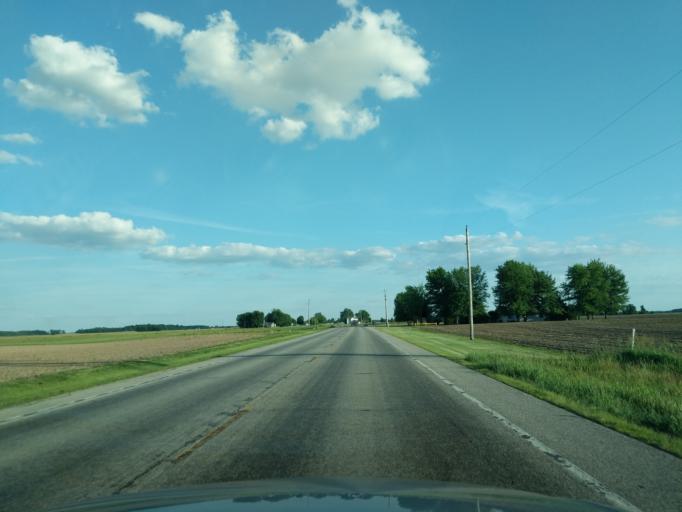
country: US
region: Indiana
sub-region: Huntington County
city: Warren
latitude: 40.7616
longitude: -85.4515
